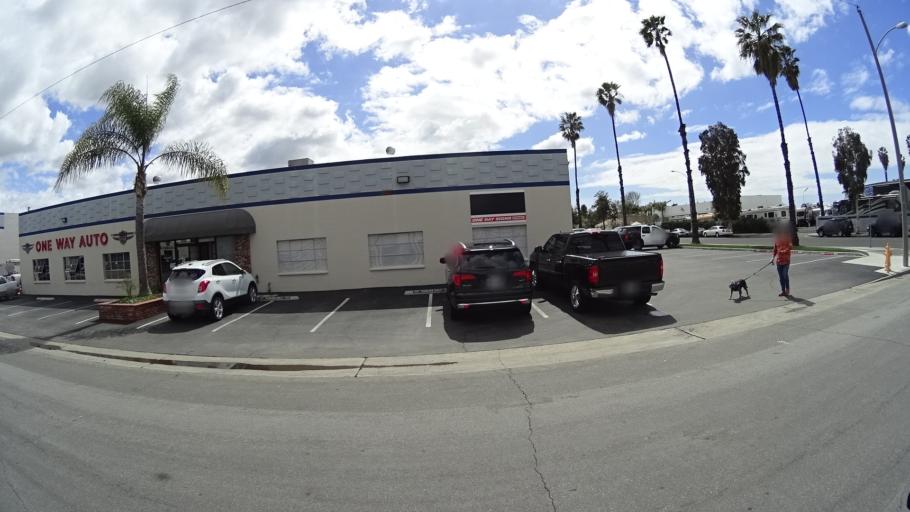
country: US
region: California
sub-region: Orange County
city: Anaheim
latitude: 33.8314
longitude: -117.9369
